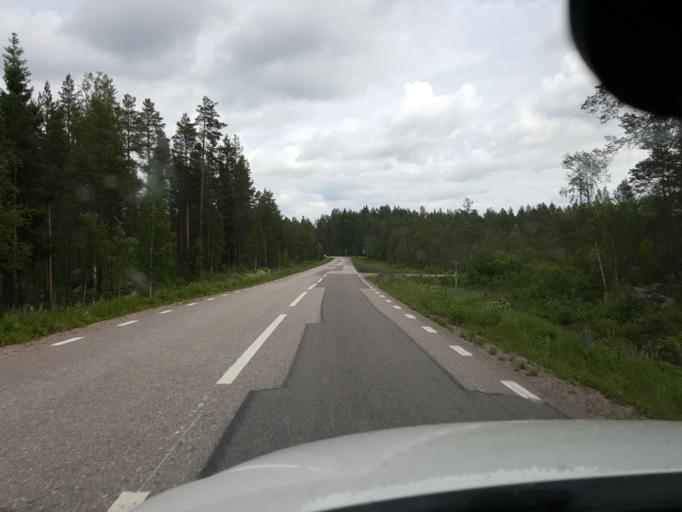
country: SE
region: Gaevleborg
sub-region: Ljusdals Kommun
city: Farila
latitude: 61.7813
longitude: 15.6020
